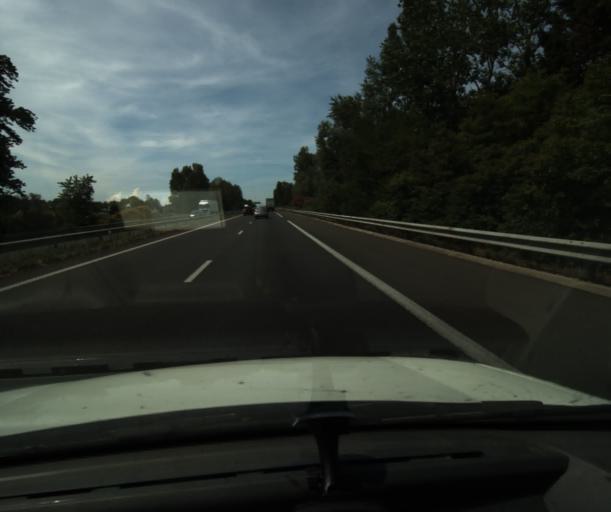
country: FR
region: Languedoc-Roussillon
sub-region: Departement de l'Aude
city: Villeneuve-la-Comptal
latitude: 43.2975
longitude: 1.9269
